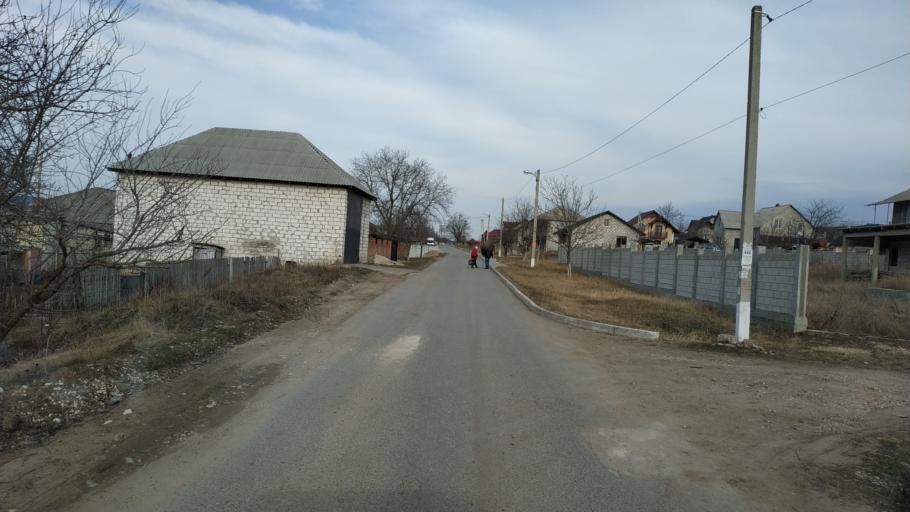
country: MD
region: Chisinau
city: Vatra
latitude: 46.9864
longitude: 28.6683
